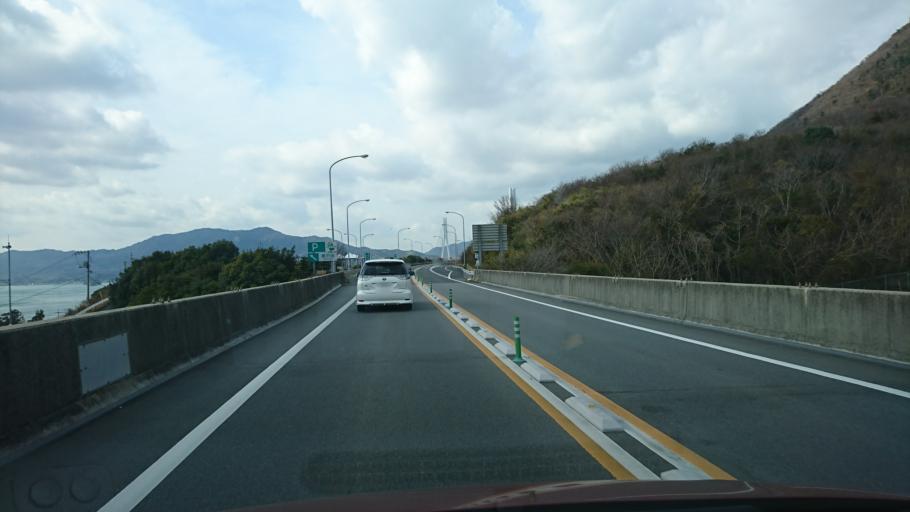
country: JP
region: Hiroshima
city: Innoshima
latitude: 34.2596
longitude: 133.0844
